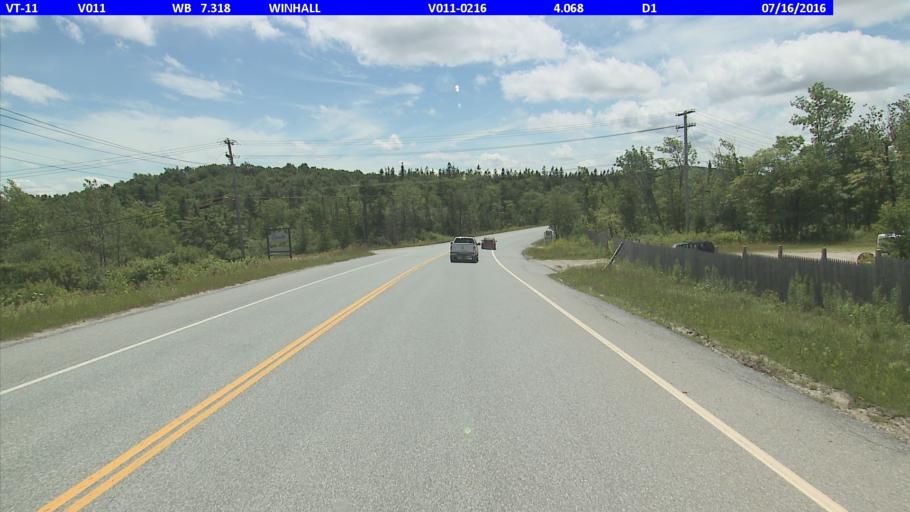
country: US
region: Vermont
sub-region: Bennington County
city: Manchester Center
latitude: 43.2073
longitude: -72.9430
